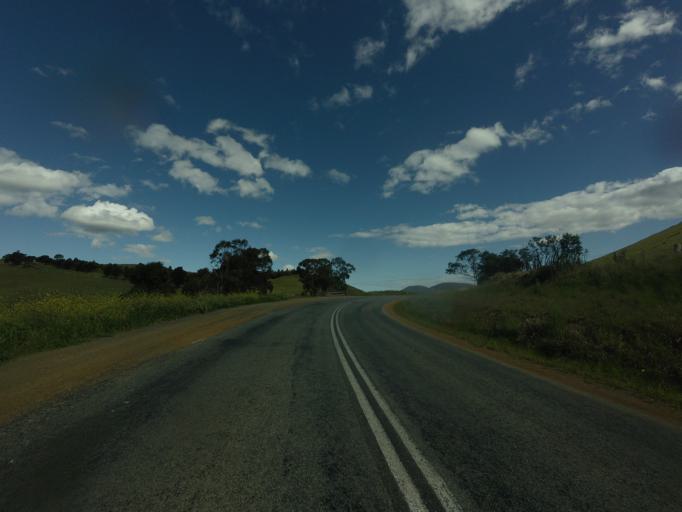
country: AU
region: Tasmania
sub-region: Brighton
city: Bridgewater
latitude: -42.5601
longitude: 147.3915
